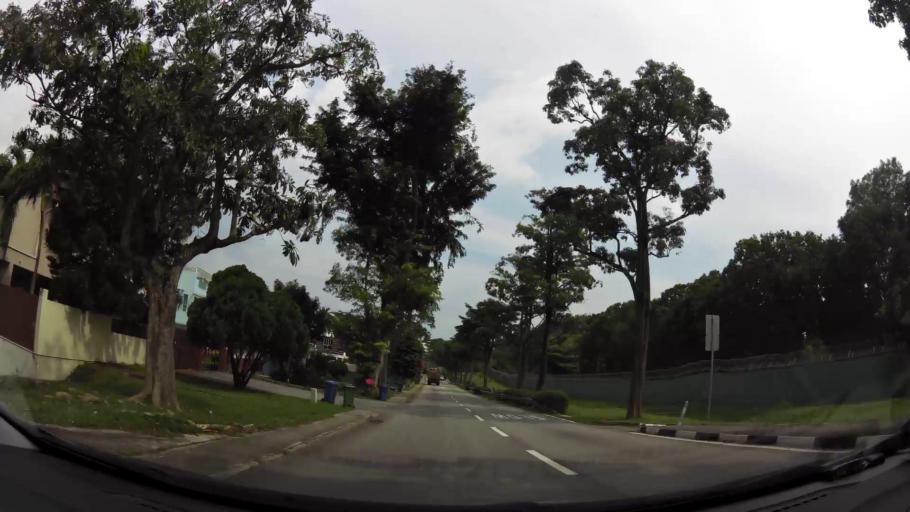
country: SG
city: Singapore
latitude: 1.3639
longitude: 103.9747
